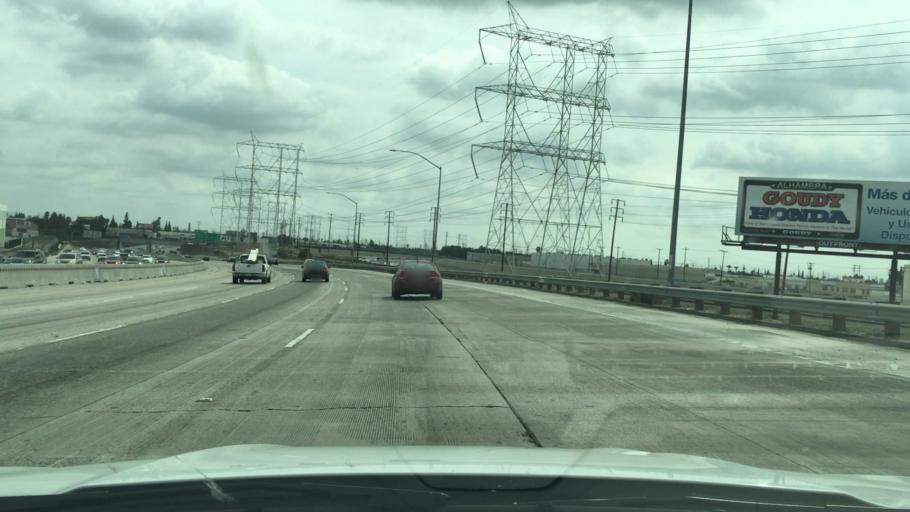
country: US
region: California
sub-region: Los Angeles County
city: Maywood
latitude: 33.9929
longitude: -118.1762
